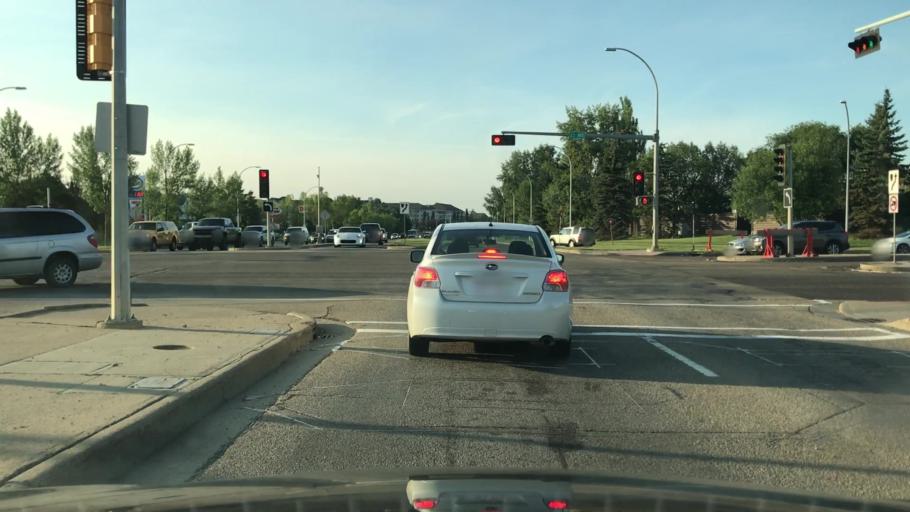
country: CA
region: Alberta
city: Beaumont
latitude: 53.4545
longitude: -113.4199
